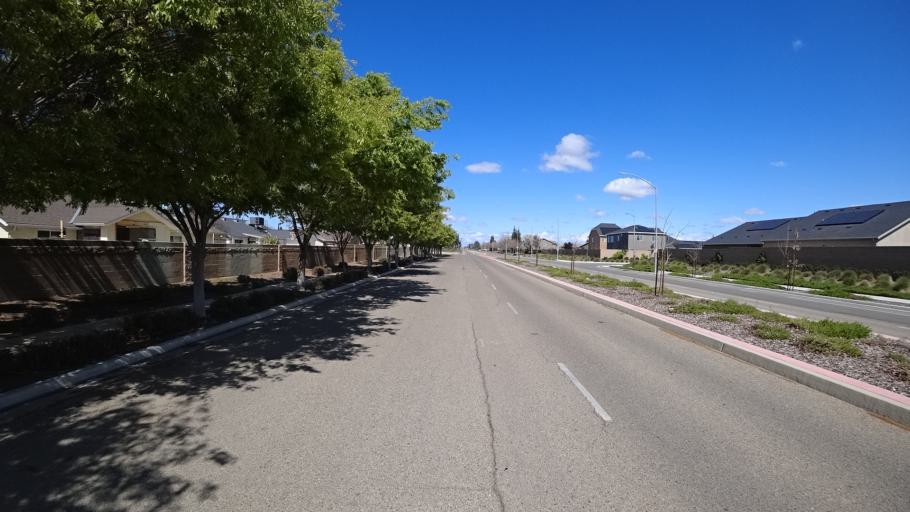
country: US
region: California
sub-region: Fresno County
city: West Park
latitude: 36.7597
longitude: -119.8894
